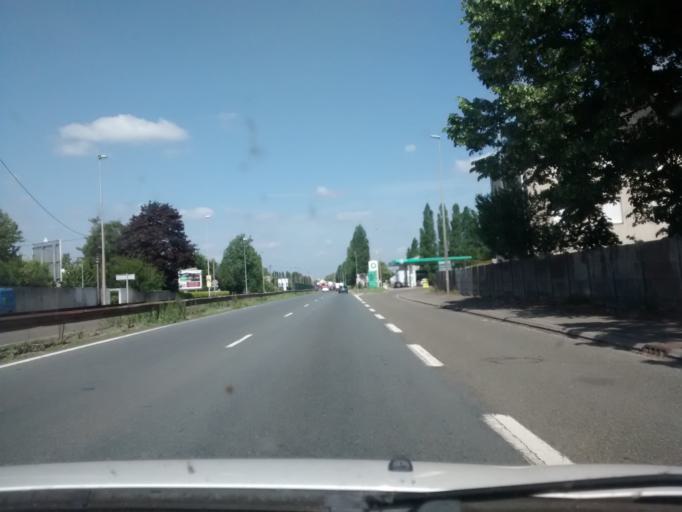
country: FR
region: Ile-de-France
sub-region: Departement des Yvelines
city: Elancourt
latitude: 48.7691
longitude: 1.9827
